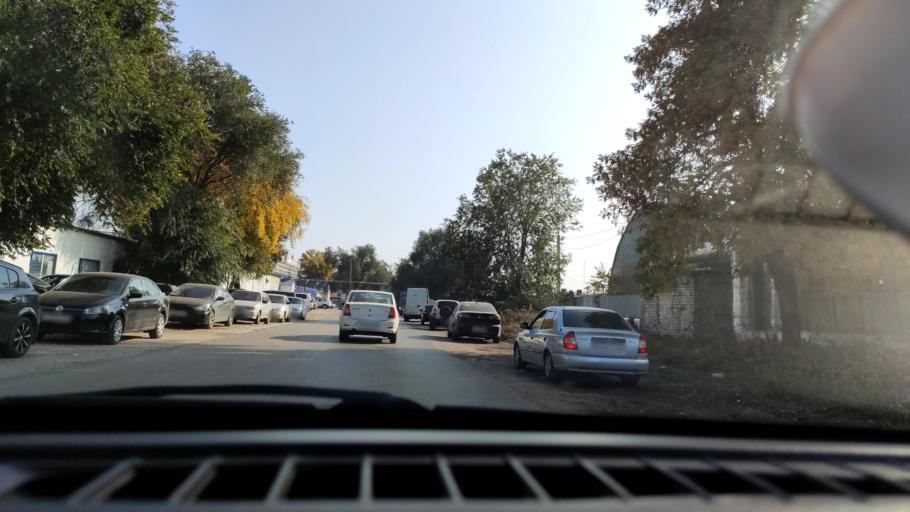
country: RU
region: Samara
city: Samara
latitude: 53.1987
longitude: 50.2570
